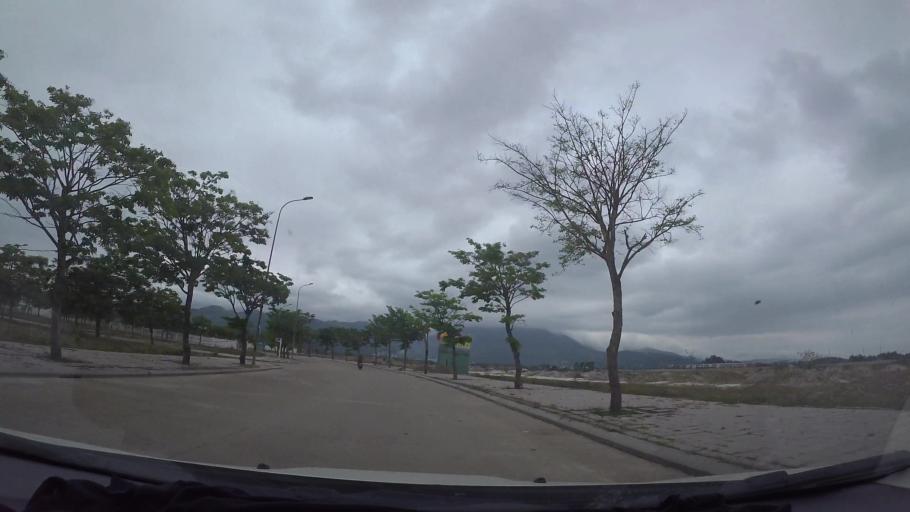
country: VN
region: Da Nang
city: Lien Chieu
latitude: 16.1047
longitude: 108.1219
